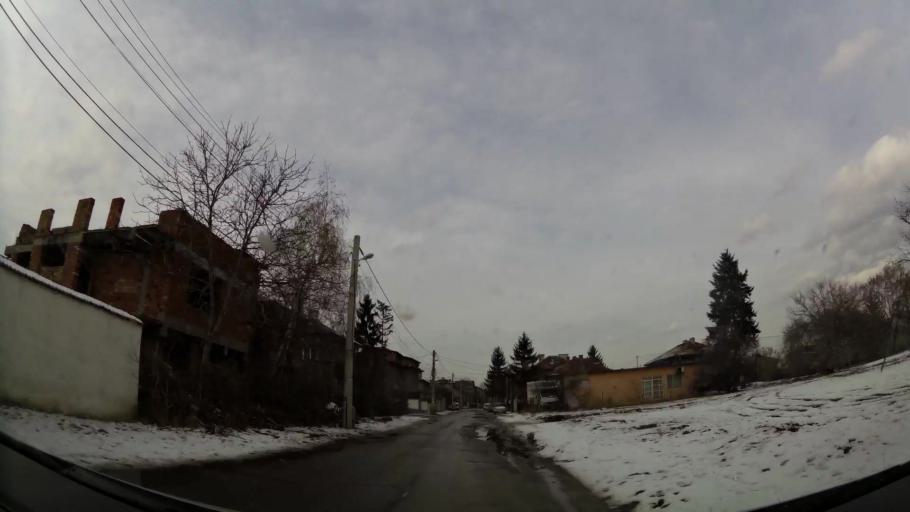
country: BG
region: Sofia-Capital
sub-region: Stolichna Obshtina
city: Sofia
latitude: 42.6978
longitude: 23.3817
